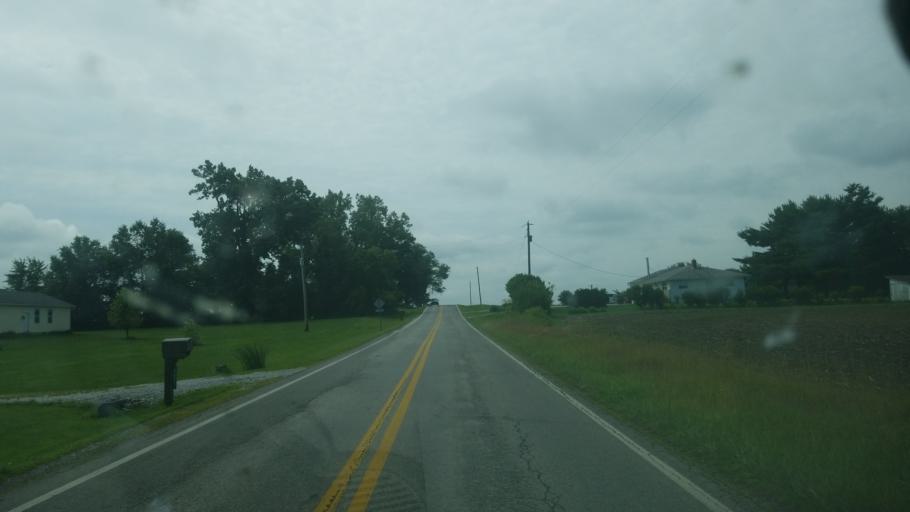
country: US
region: Ohio
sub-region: Franklin County
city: New Albany
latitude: 40.1376
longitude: -82.7610
